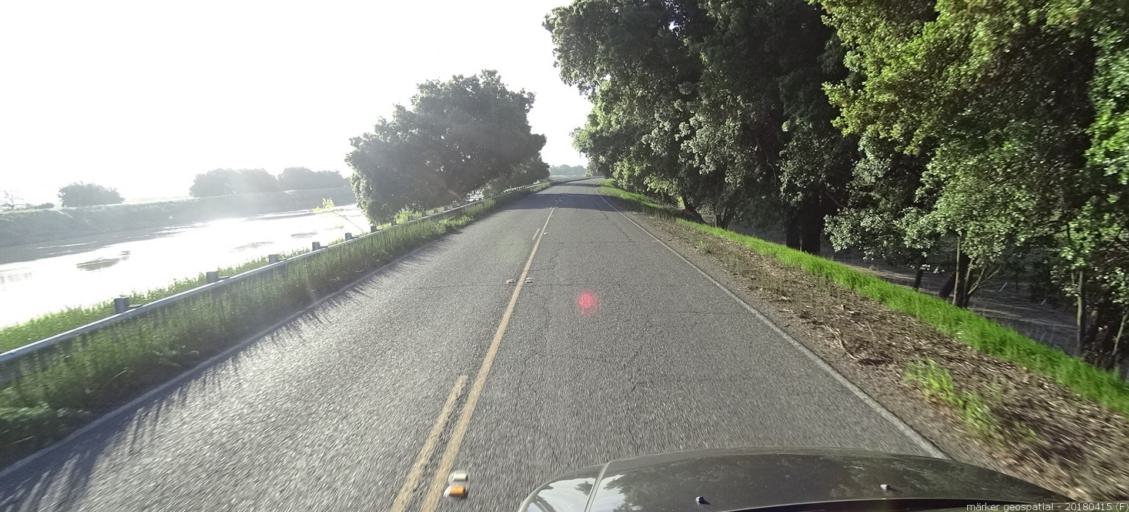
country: US
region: California
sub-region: Sacramento County
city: Walnut Grove
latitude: 38.2821
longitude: -121.5508
